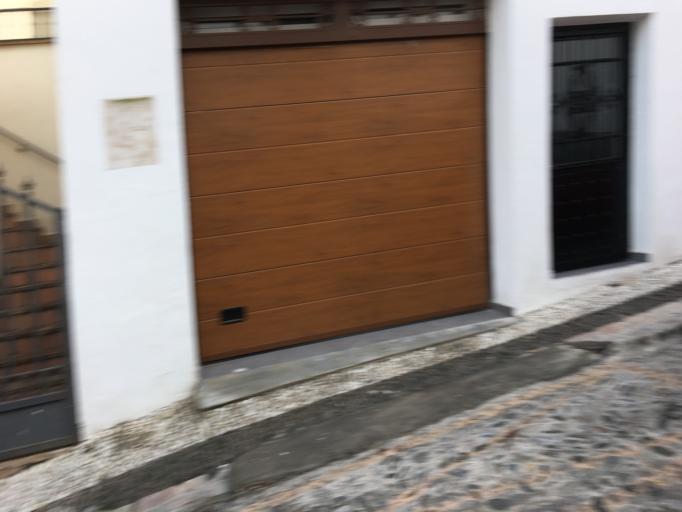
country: ES
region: Andalusia
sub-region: Provincia de Granada
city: Granada
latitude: 37.1824
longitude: -3.5957
